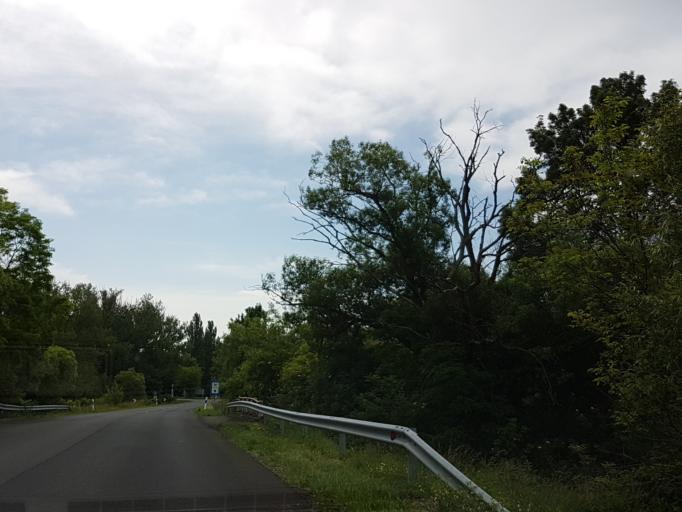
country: HU
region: Veszprem
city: Badacsonytomaj
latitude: 46.8094
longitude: 17.4646
